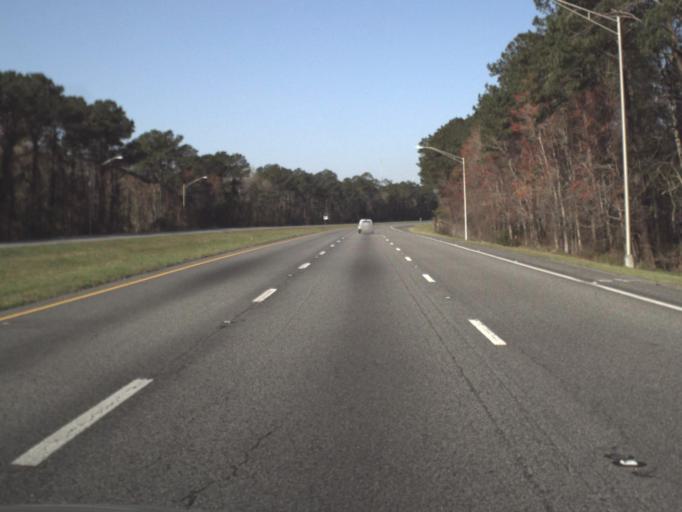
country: US
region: Florida
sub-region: Jefferson County
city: Monticello
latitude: 30.4458
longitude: -83.7357
